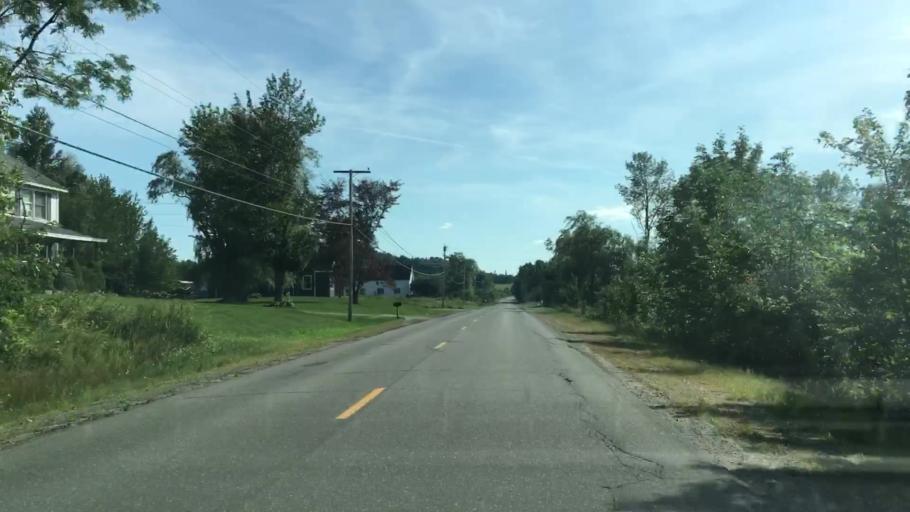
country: US
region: Maine
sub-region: Penobscot County
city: Lincoln
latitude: 45.3267
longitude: -68.5318
